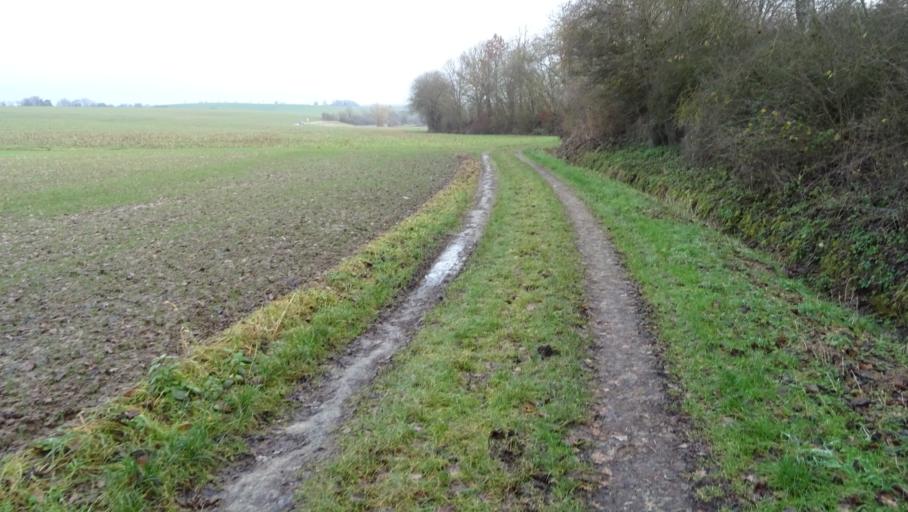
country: DE
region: Baden-Wuerttemberg
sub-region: Karlsruhe Region
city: Mosbach
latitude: 49.3607
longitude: 9.1862
